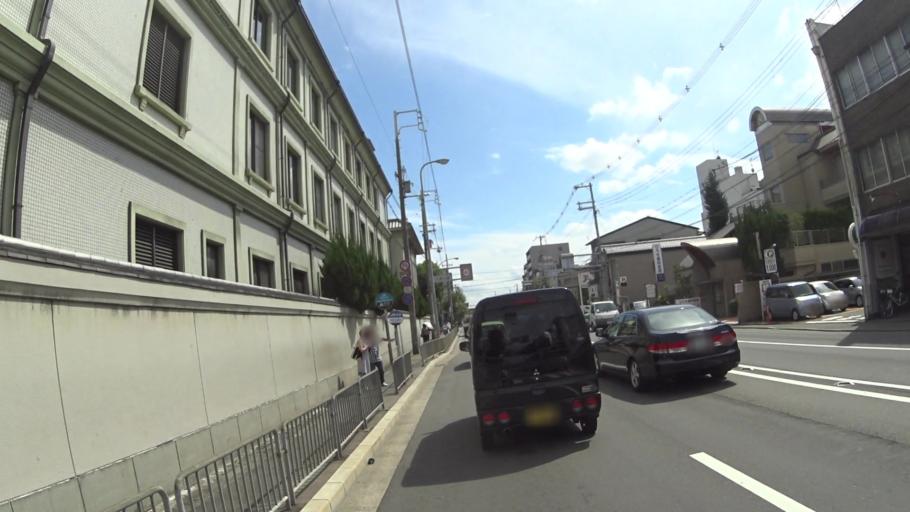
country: JP
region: Kyoto
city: Kyoto
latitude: 34.9902
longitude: 135.7493
